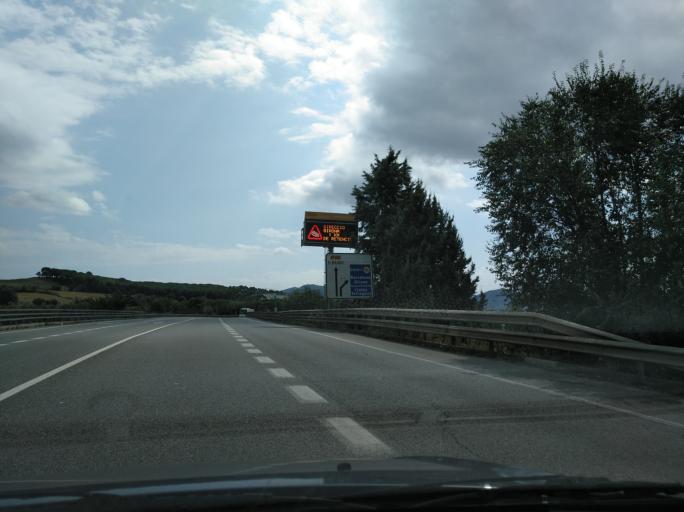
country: ES
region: Catalonia
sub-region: Provincia de Barcelona
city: Granollers
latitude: 41.5742
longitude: 2.2824
